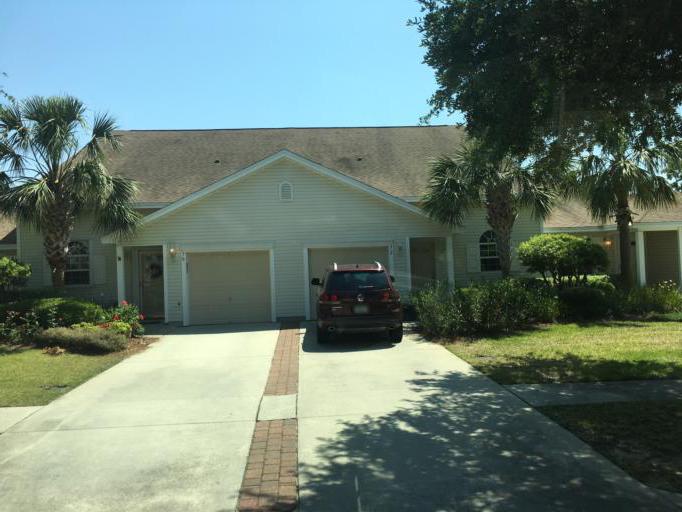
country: US
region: Florida
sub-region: Bay County
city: Panama City Beach
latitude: 30.2196
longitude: -85.8571
